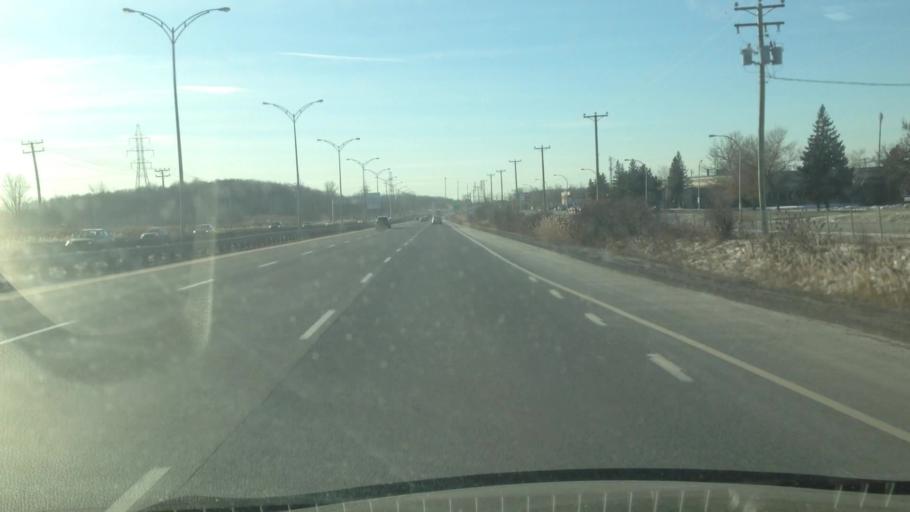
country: CA
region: Quebec
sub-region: Laurentides
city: Boisbriand
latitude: 45.6120
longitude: -73.8536
